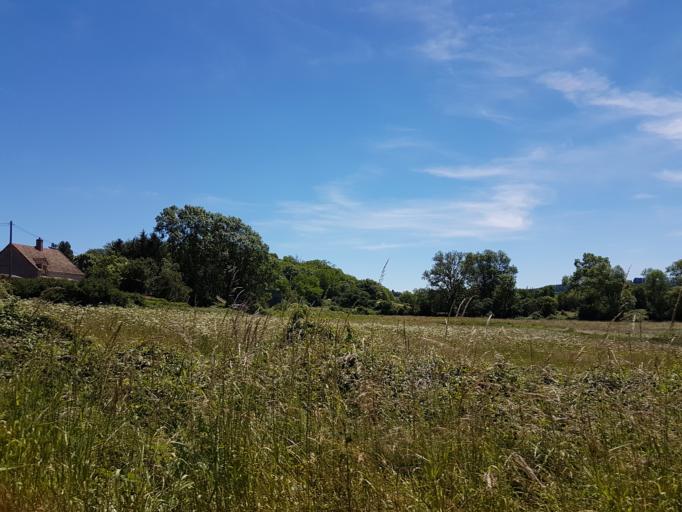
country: FR
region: Bourgogne
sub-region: Departement de Saone-et-Loire
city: Epinac
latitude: 46.9944
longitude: 4.5045
